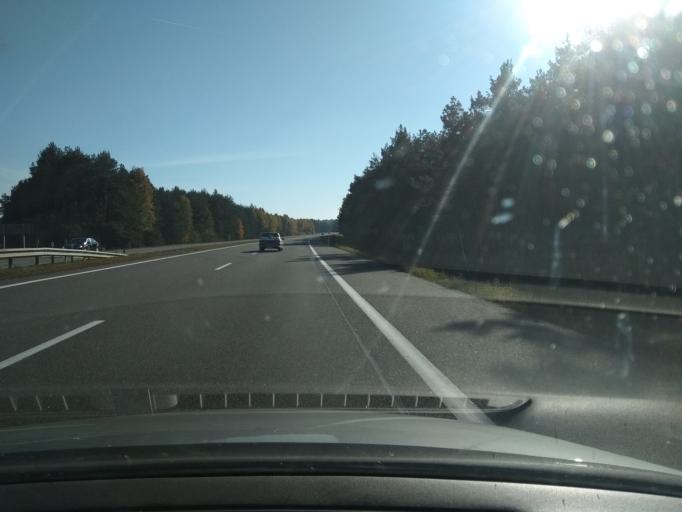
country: BY
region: Brest
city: Baranovichi
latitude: 53.0854
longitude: 25.8869
